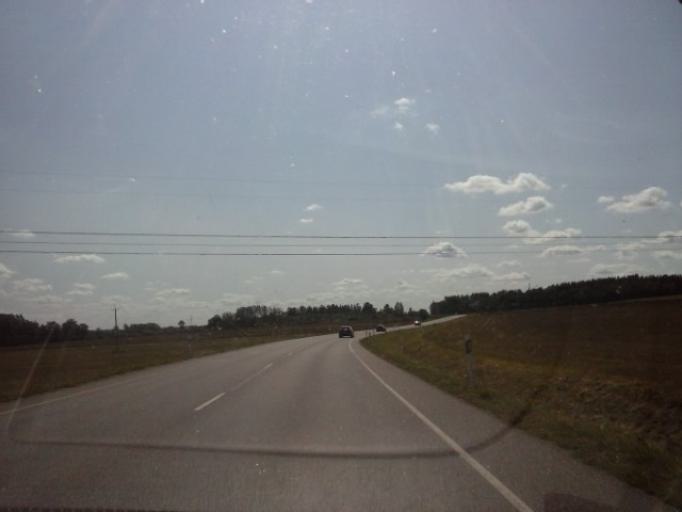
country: EE
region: Tartu
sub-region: UElenurme vald
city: Ulenurme
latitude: 58.2300
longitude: 26.7887
